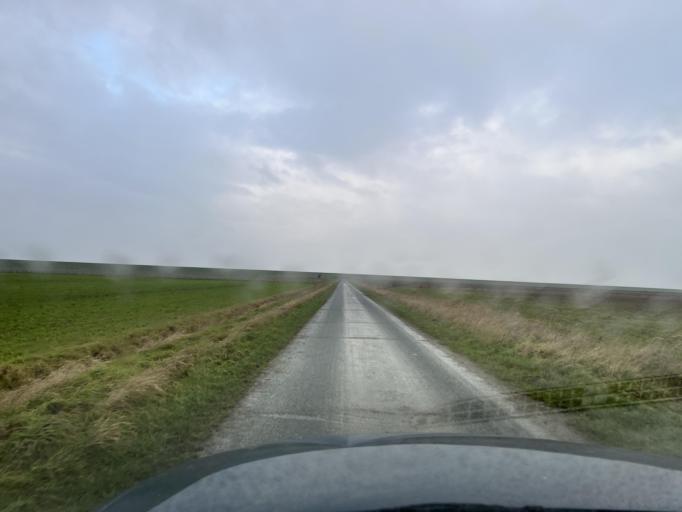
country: DE
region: Schleswig-Holstein
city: Hellschen-Heringsand-Unterschaar
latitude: 54.2225
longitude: 8.8500
